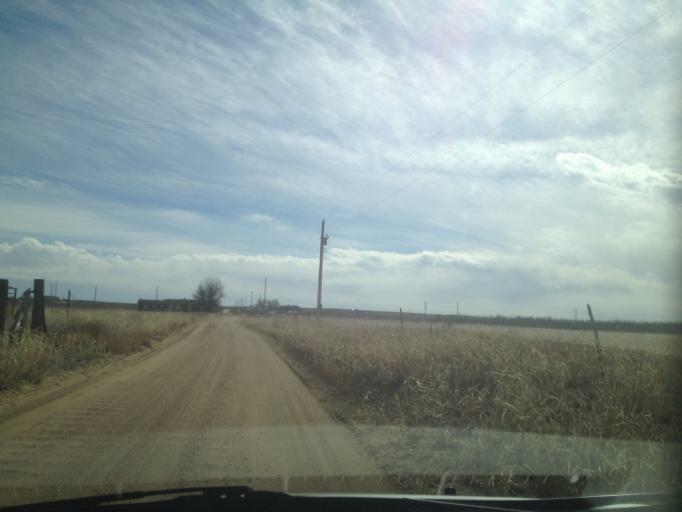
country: US
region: Colorado
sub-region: Weld County
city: Keenesburg
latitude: 40.2895
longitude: -104.2591
